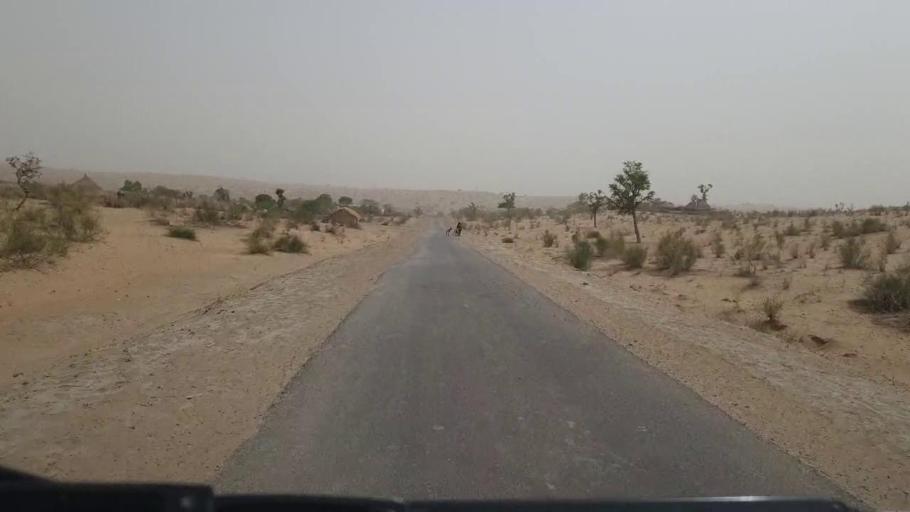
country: PK
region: Sindh
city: Islamkot
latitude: 25.2710
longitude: 70.6521
